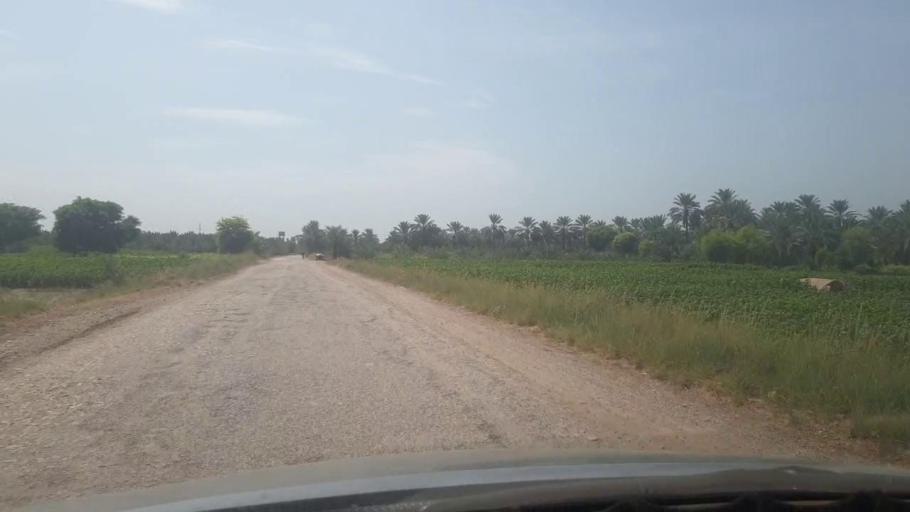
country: PK
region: Sindh
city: Bozdar
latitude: 27.2034
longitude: 68.5818
